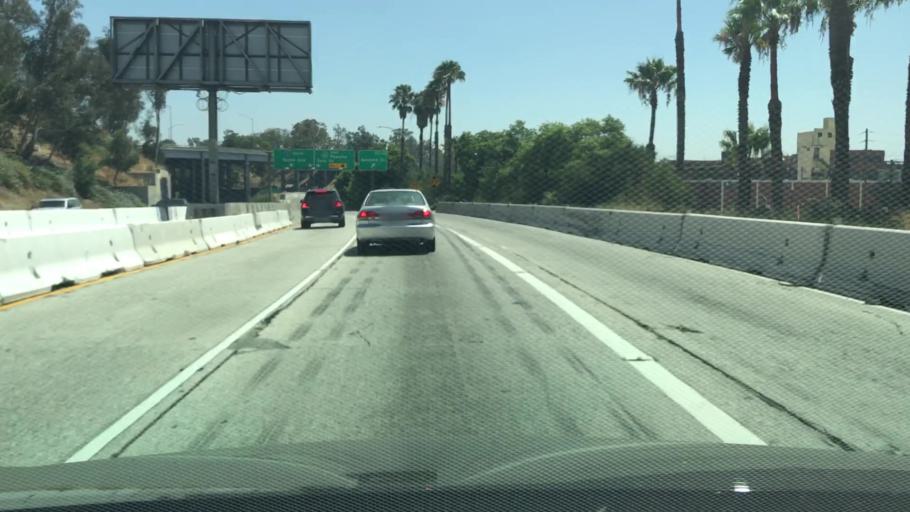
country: US
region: California
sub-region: Los Angeles County
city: Boyle Heights
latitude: 34.0368
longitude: -118.2217
